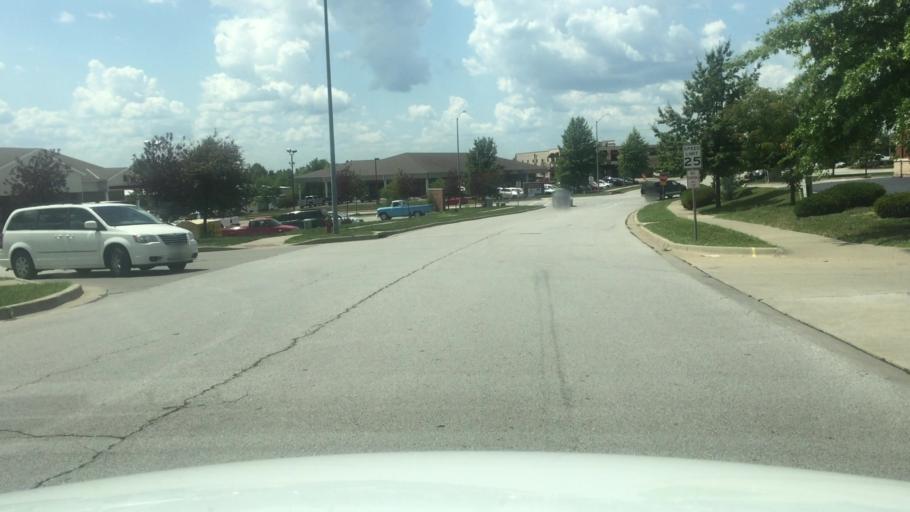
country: US
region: Missouri
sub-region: Platte County
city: Platte City
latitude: 39.3525
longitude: -94.7667
